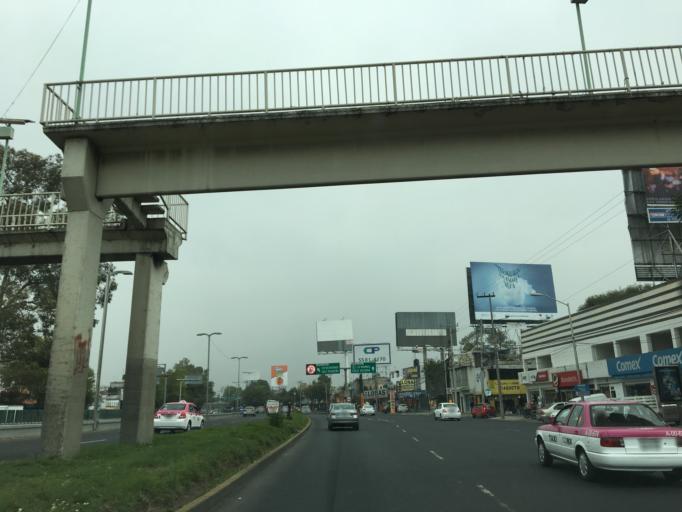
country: MX
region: Mexico City
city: Tlalpan
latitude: 19.2929
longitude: -99.1474
